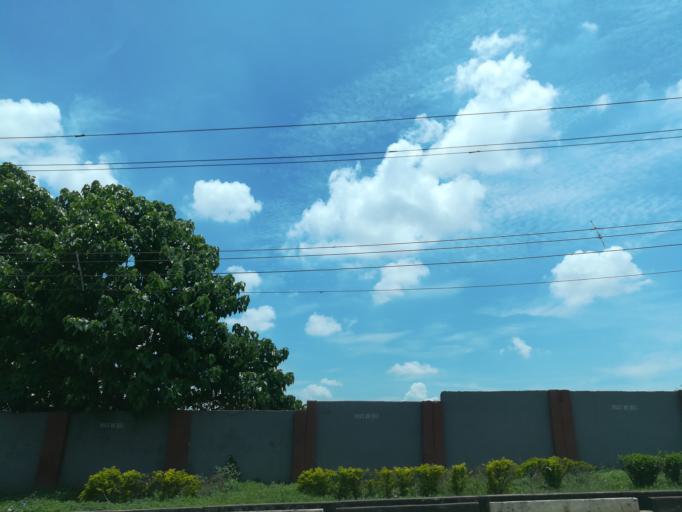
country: NG
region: Lagos
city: Ikorodu
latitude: 6.6105
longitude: 3.4999
